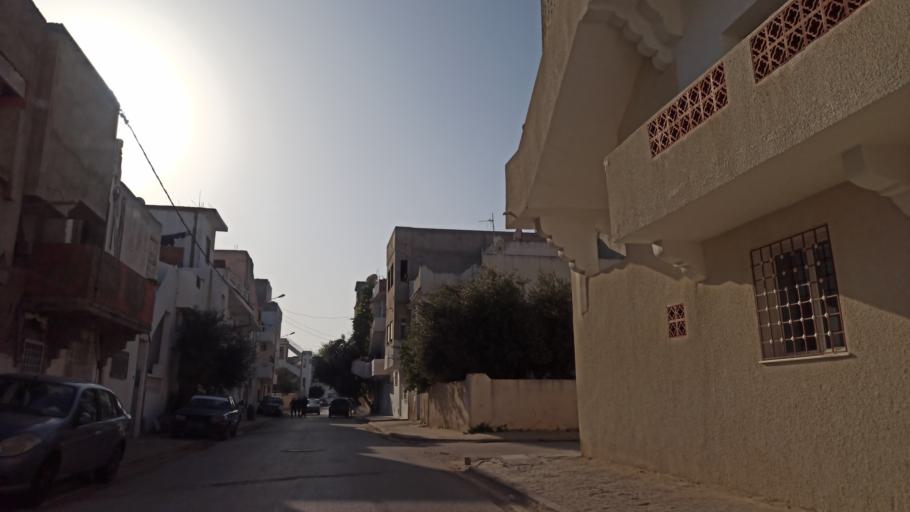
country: TN
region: Tunis
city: La Goulette
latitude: 36.8554
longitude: 10.2711
